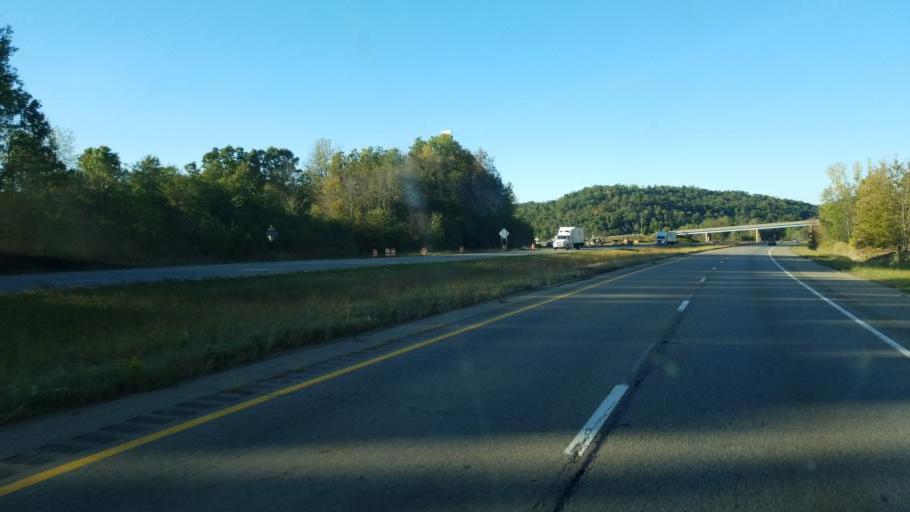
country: US
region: Ohio
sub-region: Guernsey County
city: Cambridge
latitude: 40.1428
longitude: -81.5514
